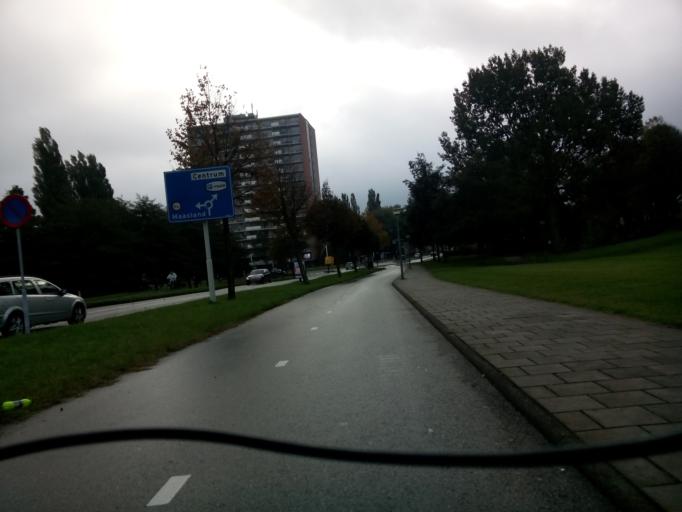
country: NL
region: South Holland
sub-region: Gemeente Maassluis
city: Maassluis
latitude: 51.9259
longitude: 4.2485
